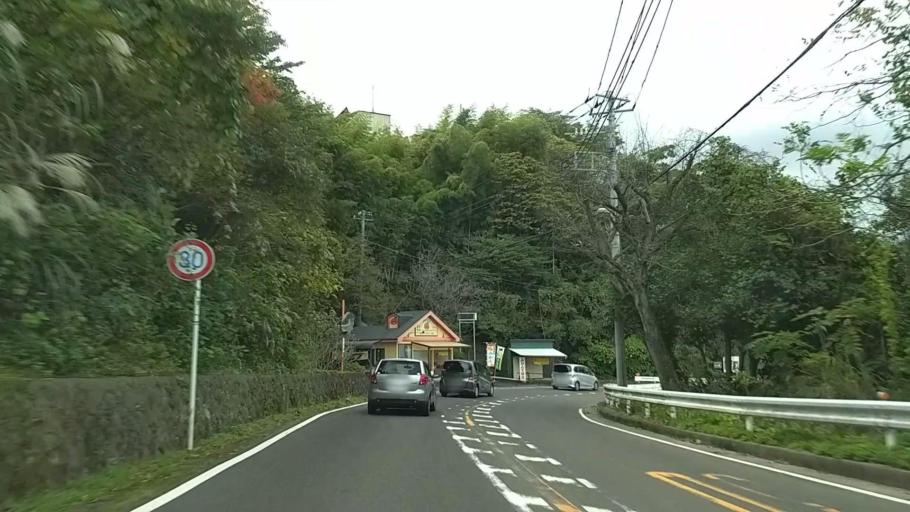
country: JP
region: Kanagawa
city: Yugawara
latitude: 35.1779
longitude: 139.1353
